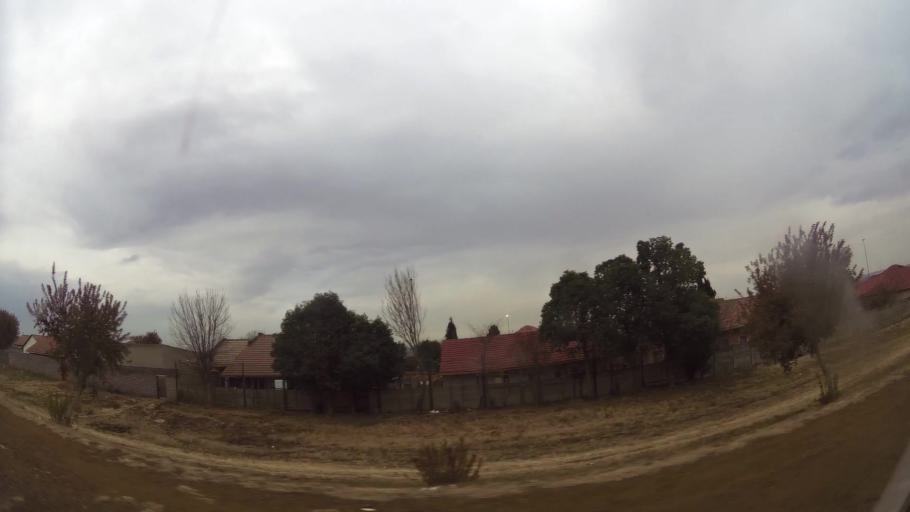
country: ZA
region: Gauteng
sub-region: Ekurhuleni Metropolitan Municipality
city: Germiston
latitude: -26.3881
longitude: 28.1554
